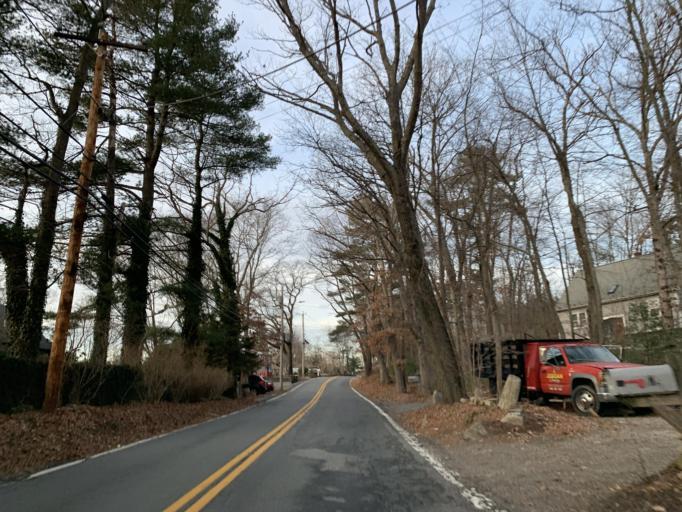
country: US
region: Rhode Island
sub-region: Providence County
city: Pascoag
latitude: 41.9492
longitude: -71.7028
